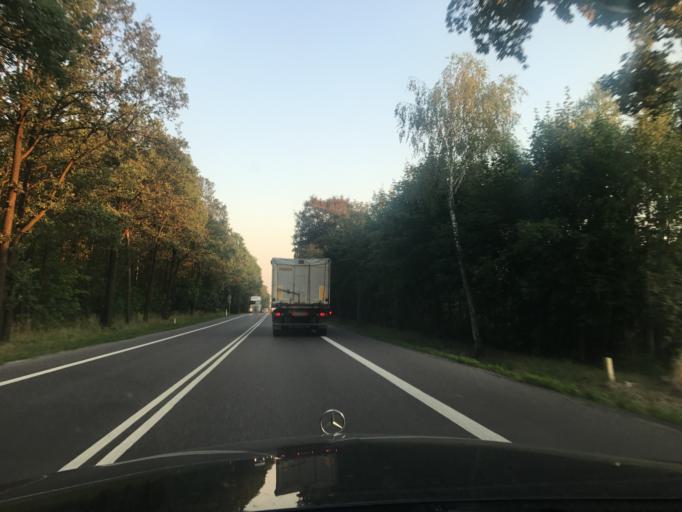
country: PL
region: Lublin Voivodeship
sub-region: Powiat lubelski
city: Niemce
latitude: 51.3969
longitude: 22.6368
